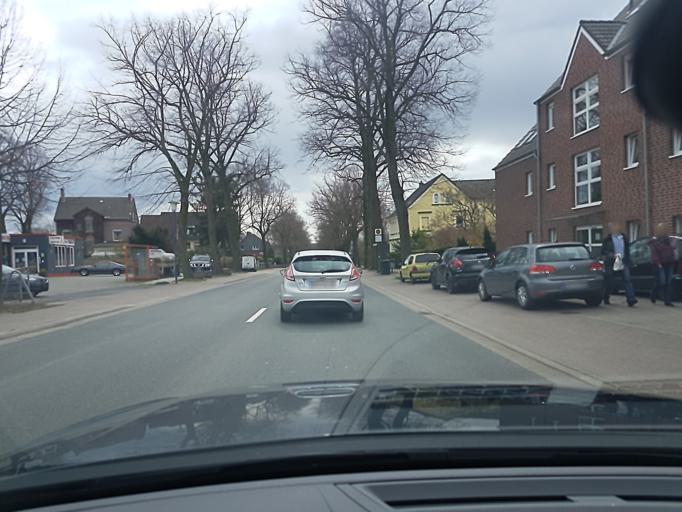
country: DE
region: North Rhine-Westphalia
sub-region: Regierungsbezirk Arnsberg
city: Unna
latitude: 51.5623
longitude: 7.6800
